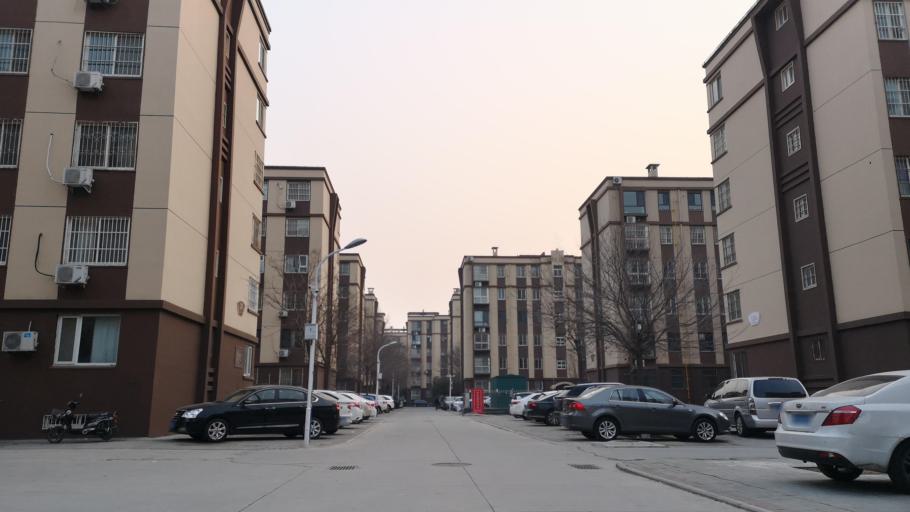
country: CN
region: Henan Sheng
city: Zhongyuanlu
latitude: 35.7869
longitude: 115.0806
